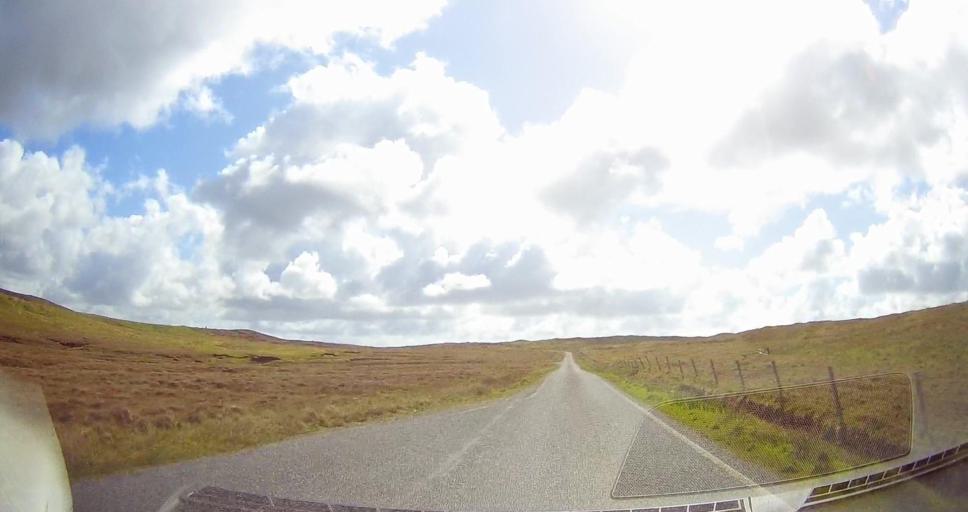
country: GB
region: Scotland
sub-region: Shetland Islands
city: Lerwick
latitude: 60.5039
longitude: -1.3924
